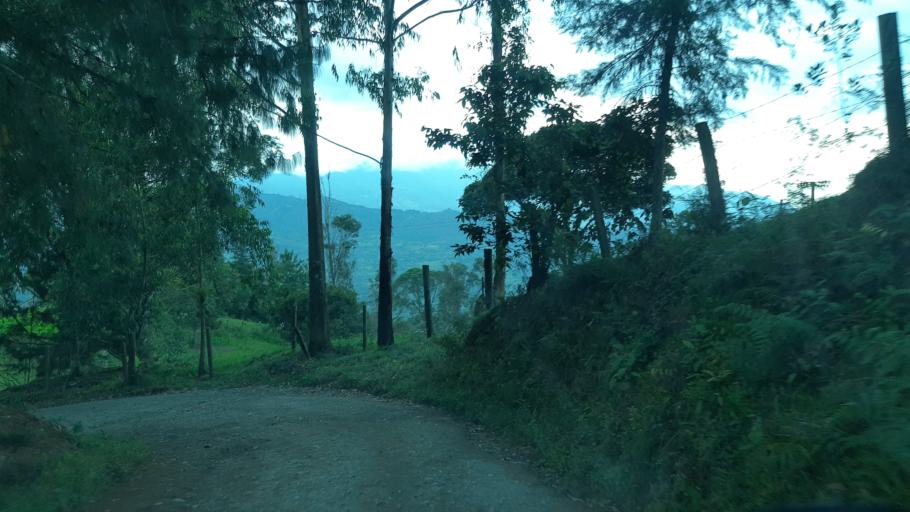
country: CO
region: Boyaca
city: Garagoa
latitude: 5.1115
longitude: -73.3524
